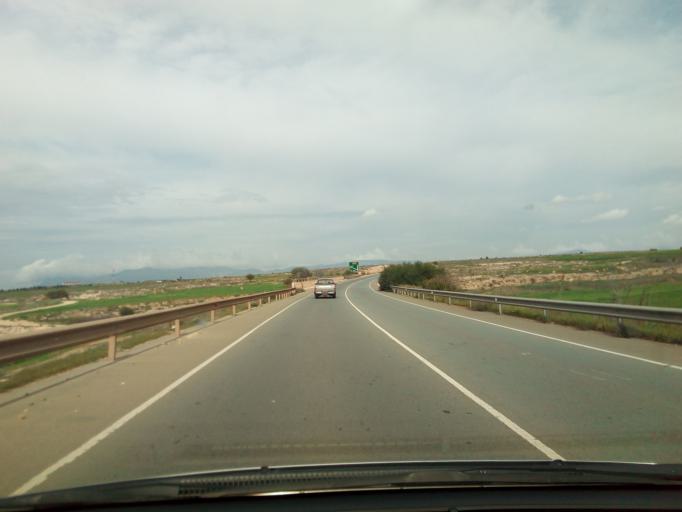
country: CY
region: Lefkosia
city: Akaki
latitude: 35.1558
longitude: 33.1558
